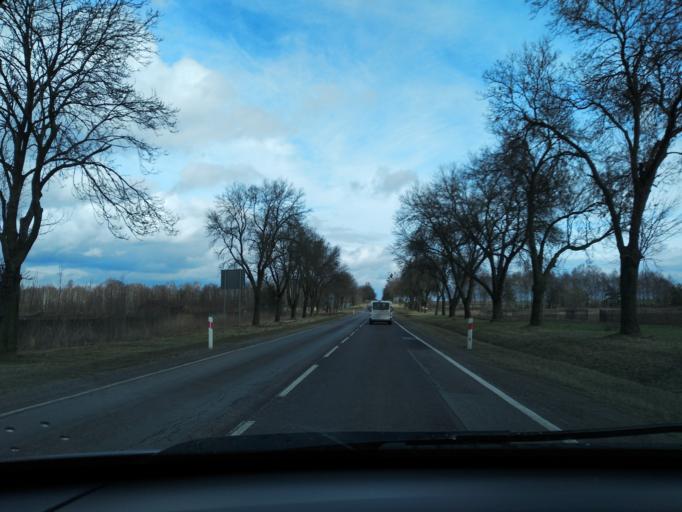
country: PL
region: Lodz Voivodeship
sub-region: Powiat zgierski
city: Strykow
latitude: 51.8659
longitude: 19.5124
